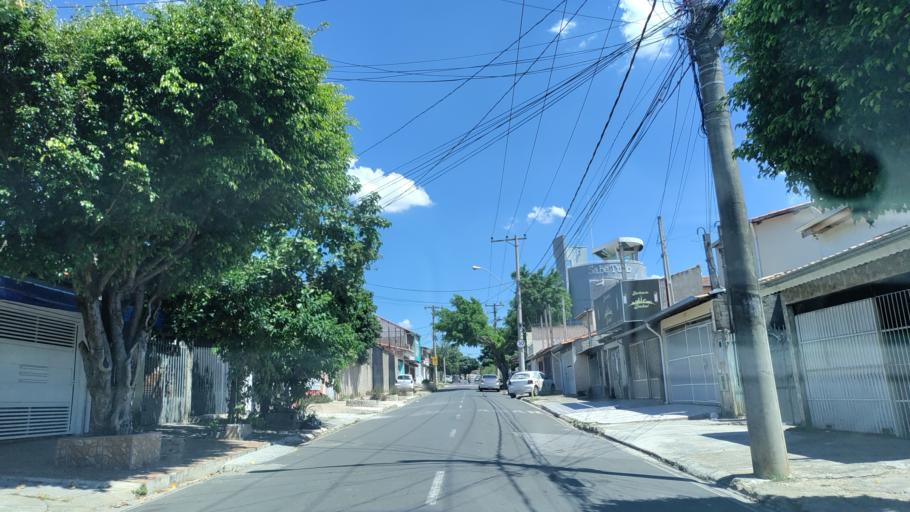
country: BR
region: Sao Paulo
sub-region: Sorocaba
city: Sorocaba
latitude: -23.4573
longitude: -47.4661
